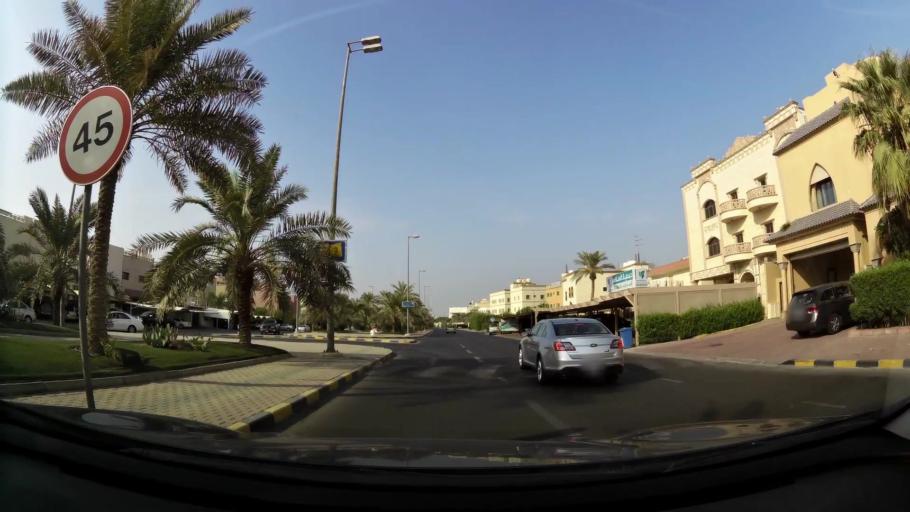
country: KW
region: Al Asimah
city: Ash Shamiyah
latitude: 29.3204
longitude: 47.9829
